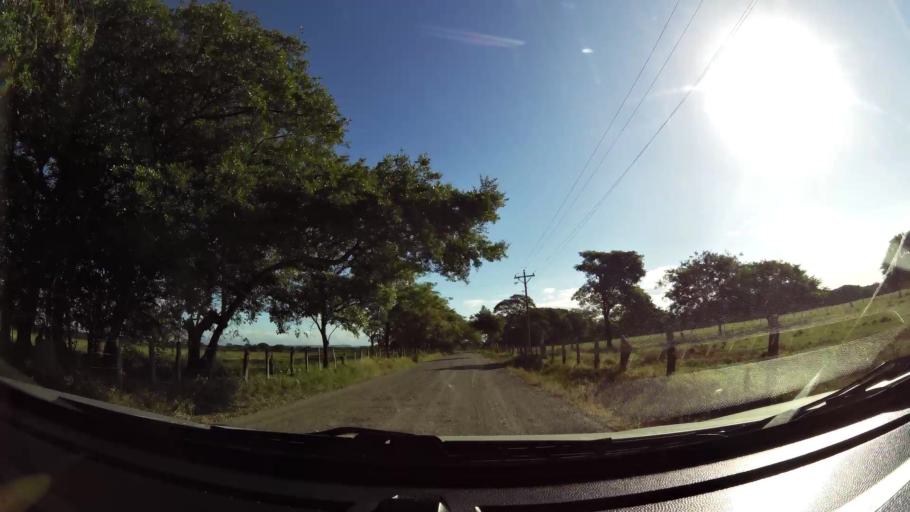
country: CR
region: Guanacaste
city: Sardinal
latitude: 10.4822
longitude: -85.5958
